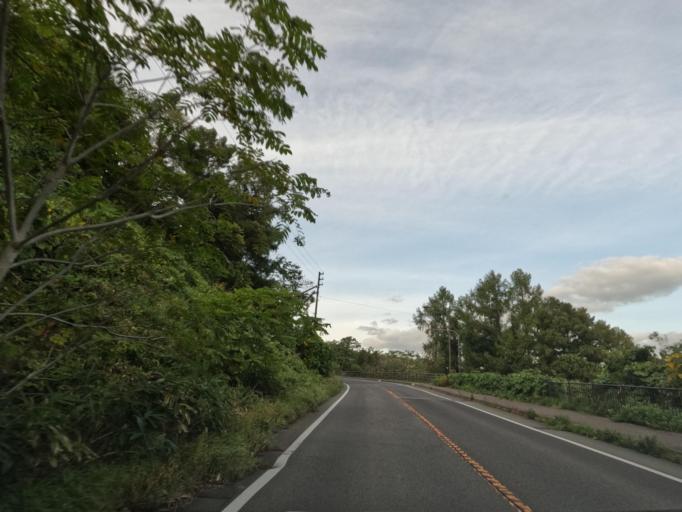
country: JP
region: Hokkaido
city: Date
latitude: 42.5284
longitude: 140.8619
